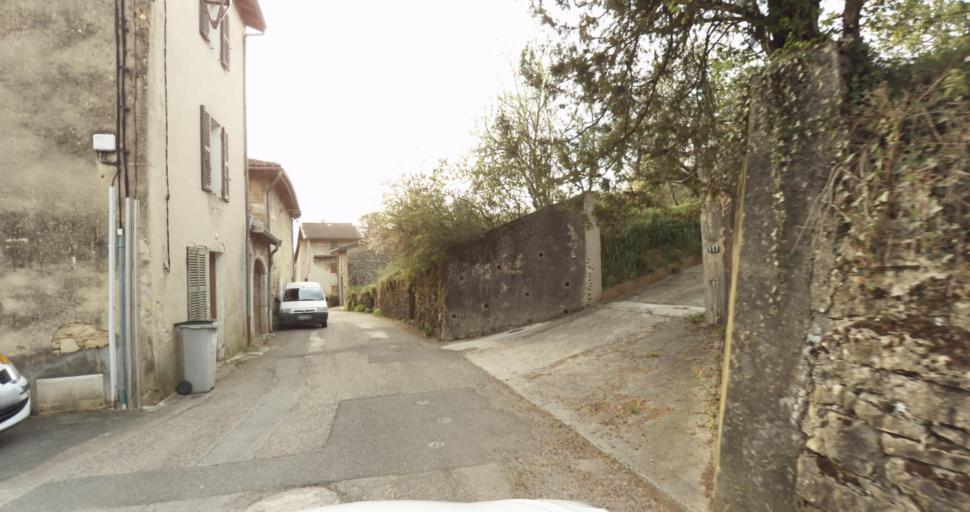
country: FR
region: Rhone-Alpes
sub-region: Departement de l'Ain
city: Amberieu-en-Bugey
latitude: 45.9566
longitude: 5.3694
